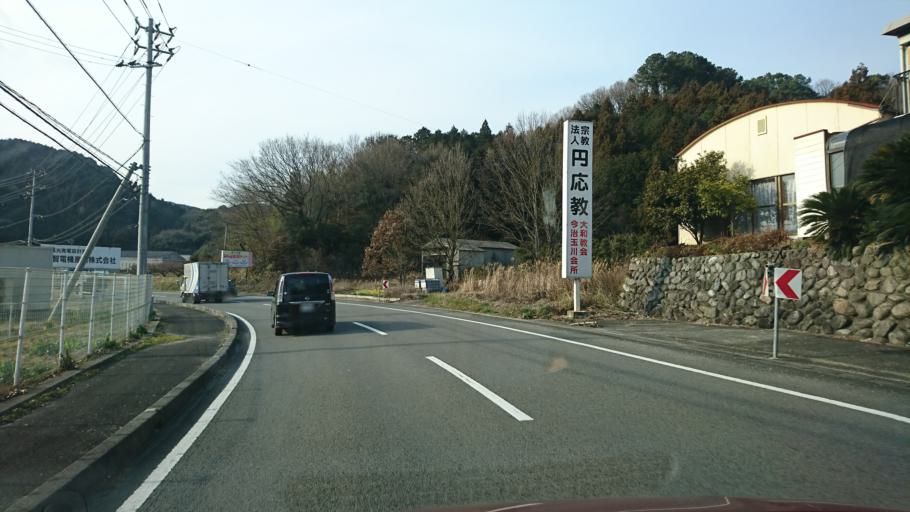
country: JP
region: Ehime
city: Hojo
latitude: 33.9965
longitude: 132.9241
